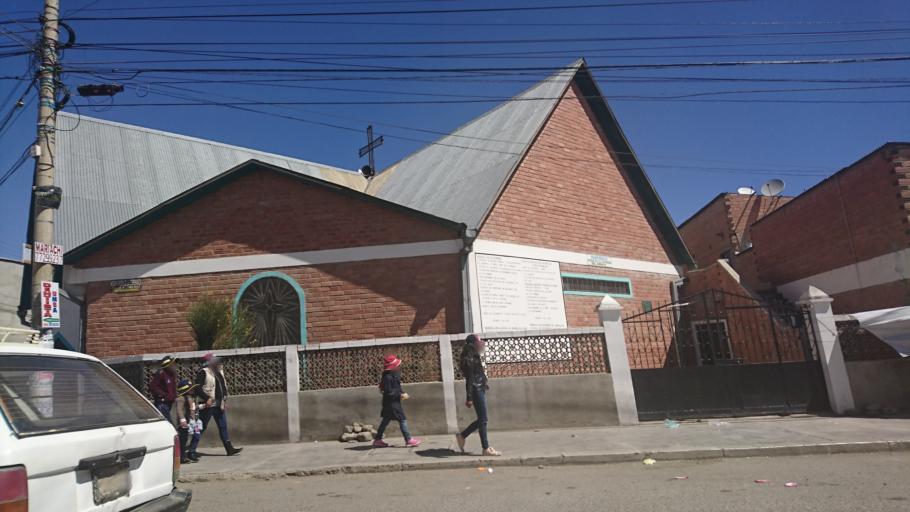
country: BO
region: La Paz
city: La Paz
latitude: -16.5367
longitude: -68.1879
